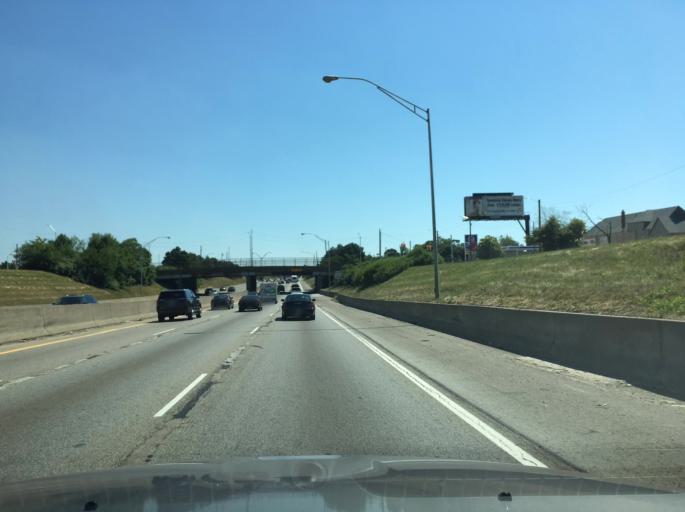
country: US
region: Michigan
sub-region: Wayne County
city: Hamtramck
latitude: 42.3737
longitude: -83.0480
